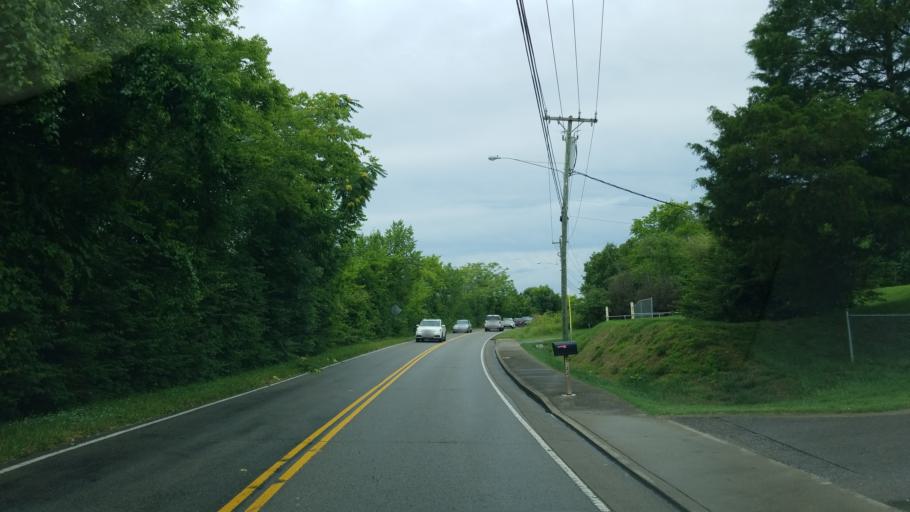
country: US
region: Tennessee
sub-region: Rutherford County
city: La Vergne
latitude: 36.0504
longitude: -86.6652
